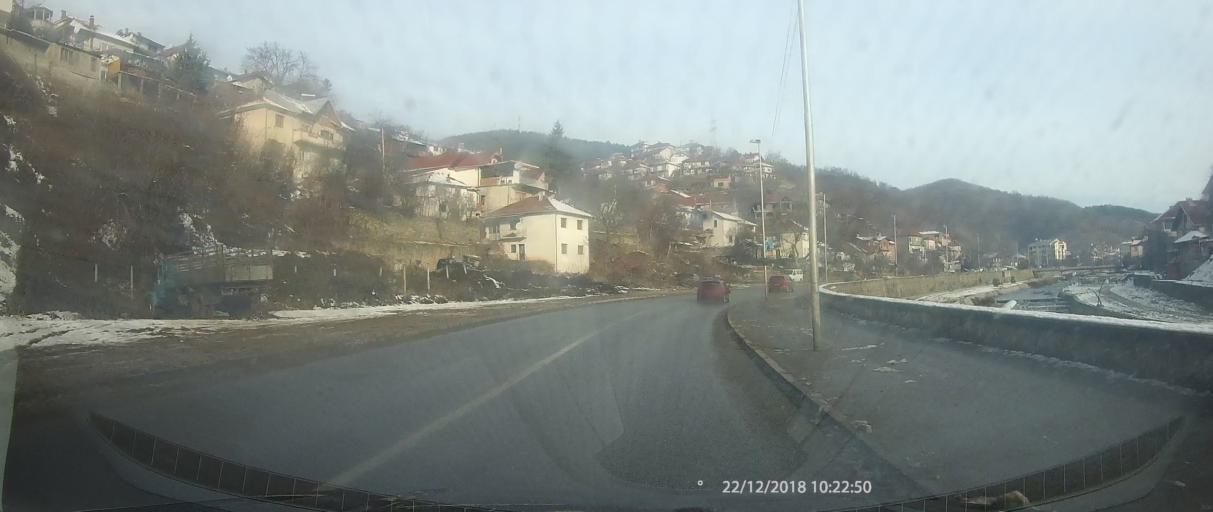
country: MK
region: Kriva Palanka
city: Kriva Palanka
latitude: 42.2045
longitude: 22.3332
